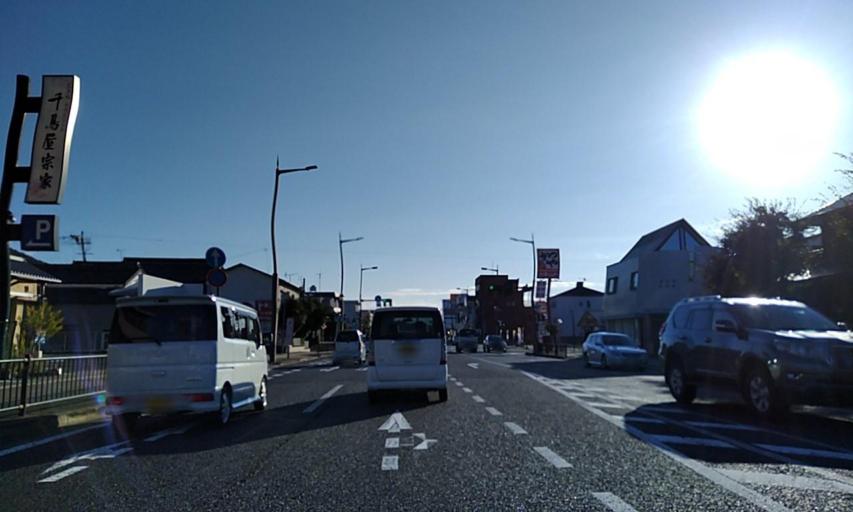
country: JP
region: Wakayama
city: Kainan
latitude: 34.1588
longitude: 135.2015
